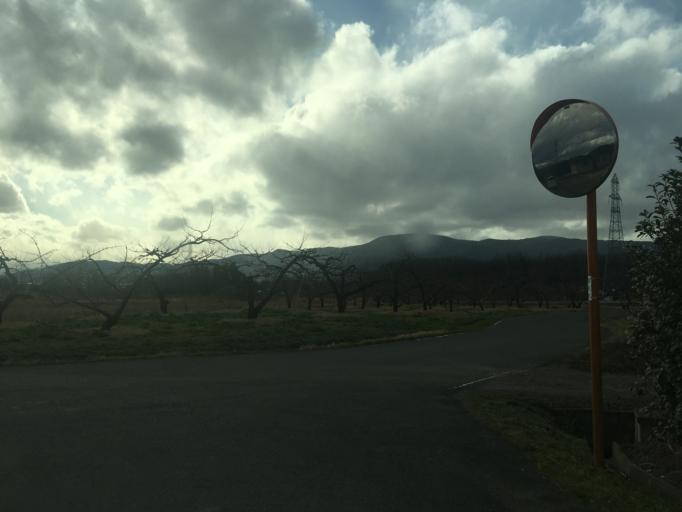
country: JP
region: Fukushima
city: Yanagawamachi-saiwaicho
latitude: 37.8824
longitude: 140.5751
